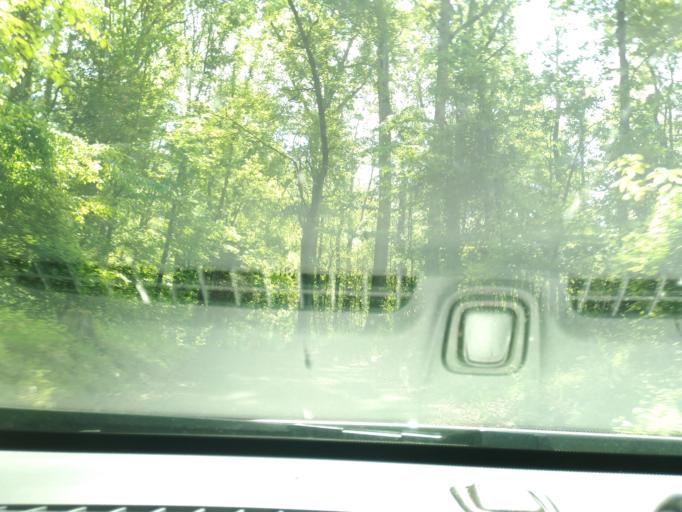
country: US
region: Maryland
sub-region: Prince George's County
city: Marlboro Meadows
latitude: 38.8514
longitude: -76.7031
